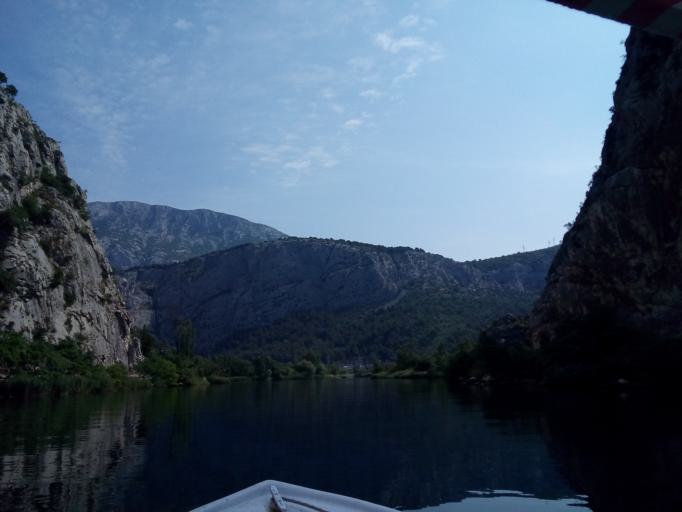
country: HR
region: Splitsko-Dalmatinska
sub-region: Grad Omis
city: Omis
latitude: 43.4492
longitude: 16.6935
